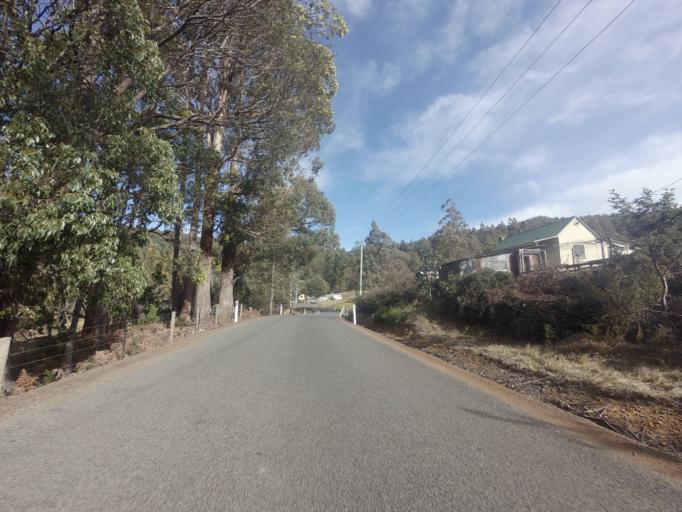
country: AU
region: Tasmania
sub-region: Kingborough
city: Margate
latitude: -43.0122
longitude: 147.1615
